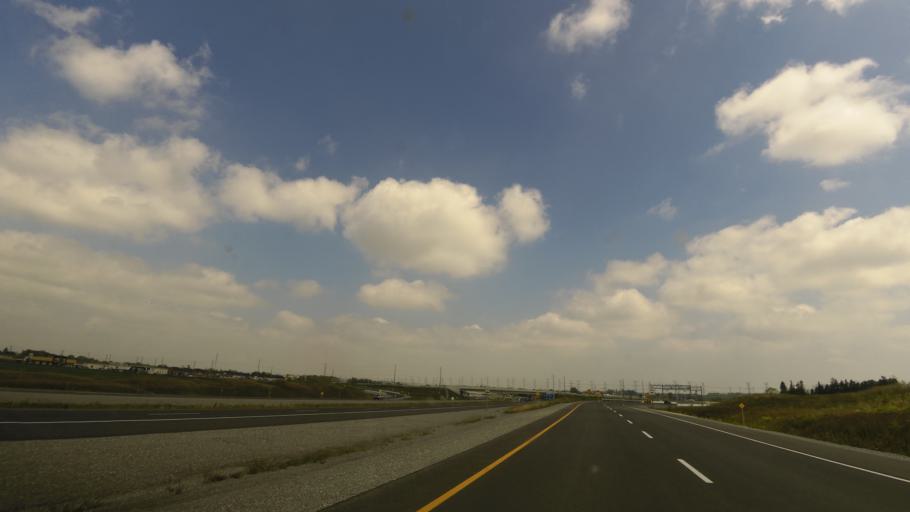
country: CA
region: Ontario
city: Ajax
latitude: 43.9474
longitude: -78.9660
